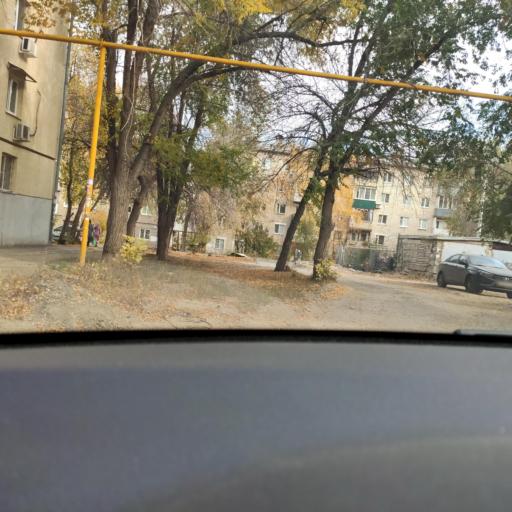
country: RU
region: Samara
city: Samara
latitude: 53.1955
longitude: 50.2097
